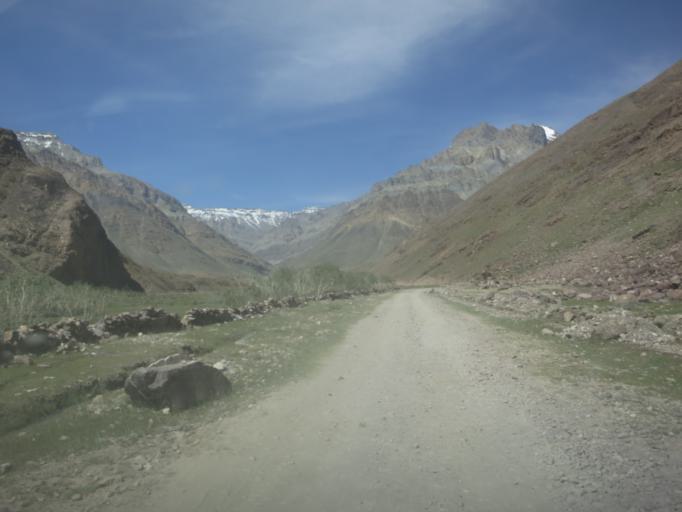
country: IN
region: Himachal Pradesh
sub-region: Kulu
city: Manali
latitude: 32.4427
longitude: 77.6870
